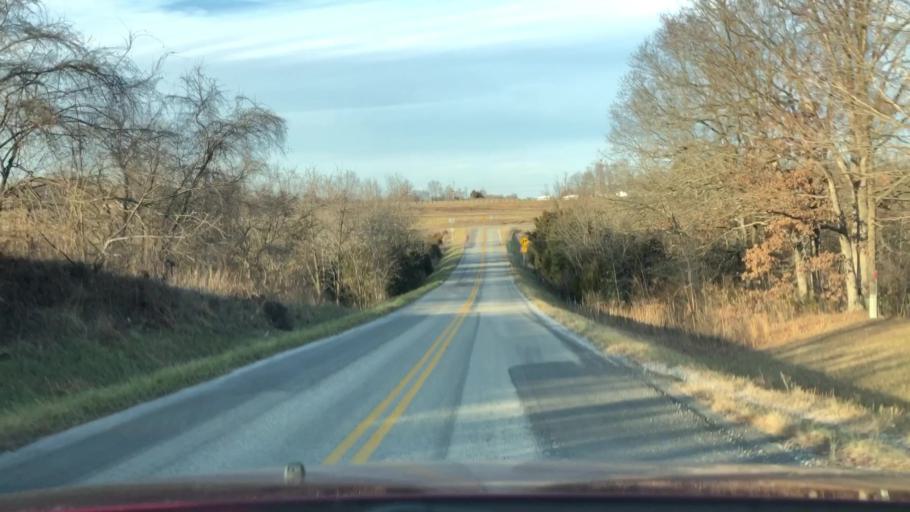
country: US
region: Missouri
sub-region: Wright County
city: Mansfield
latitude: 37.1109
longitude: -92.6295
